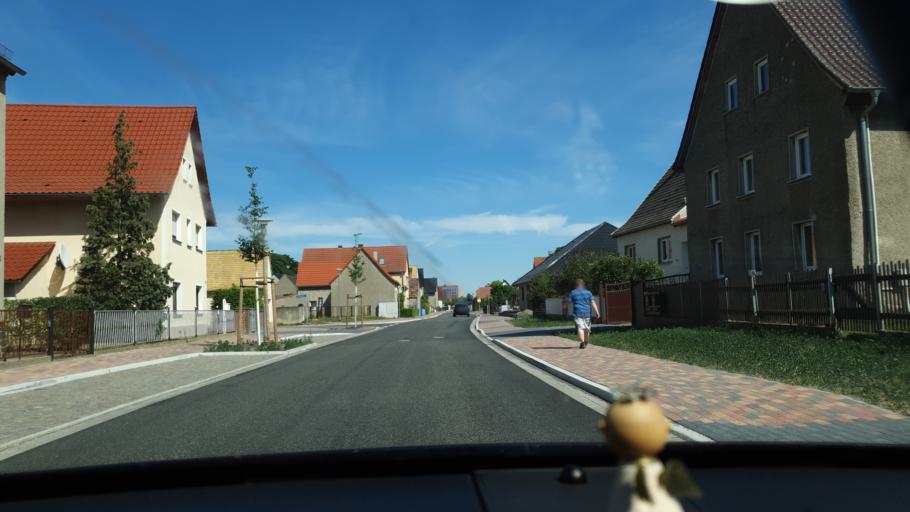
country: DE
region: Saxony
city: Doberschutz
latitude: 51.4814
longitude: 12.7820
